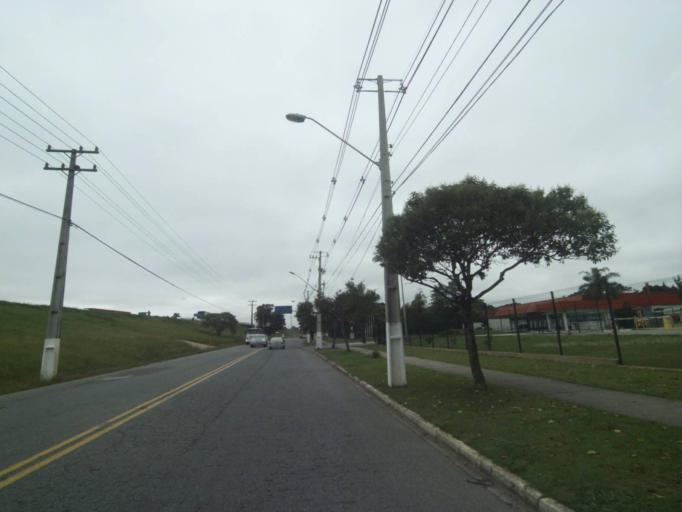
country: BR
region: Parana
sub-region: Araucaria
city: Araucaria
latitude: -25.5341
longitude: -49.3190
